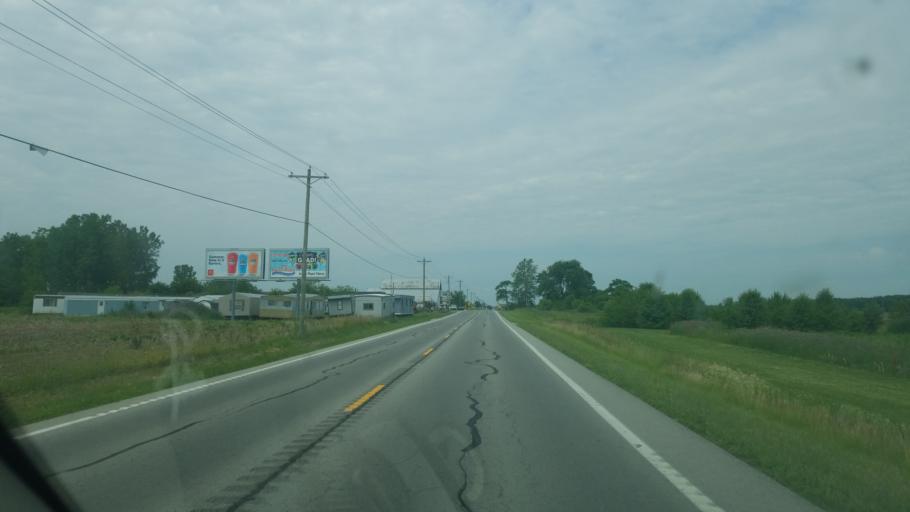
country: US
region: Ohio
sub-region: Seneca County
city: Fostoria
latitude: 41.0716
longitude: -83.4718
